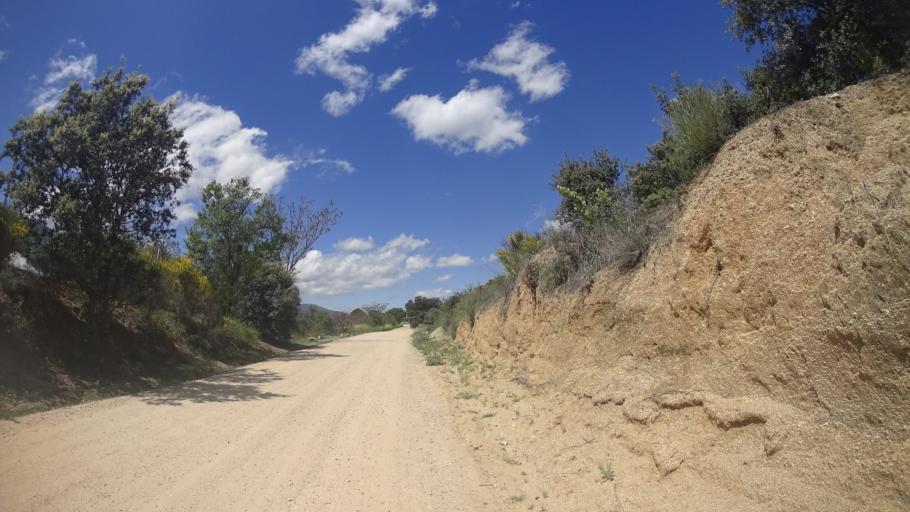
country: ES
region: Madrid
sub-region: Provincia de Madrid
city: San Martin de Valdeiglesias
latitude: 40.3619
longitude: -4.3811
